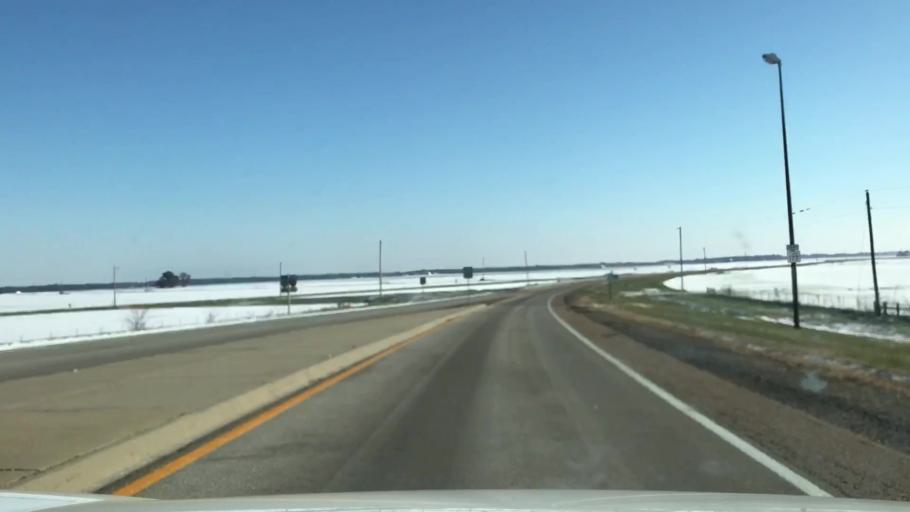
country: US
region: Illinois
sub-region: Washington County
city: Okawville
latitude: 38.4415
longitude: -89.5270
